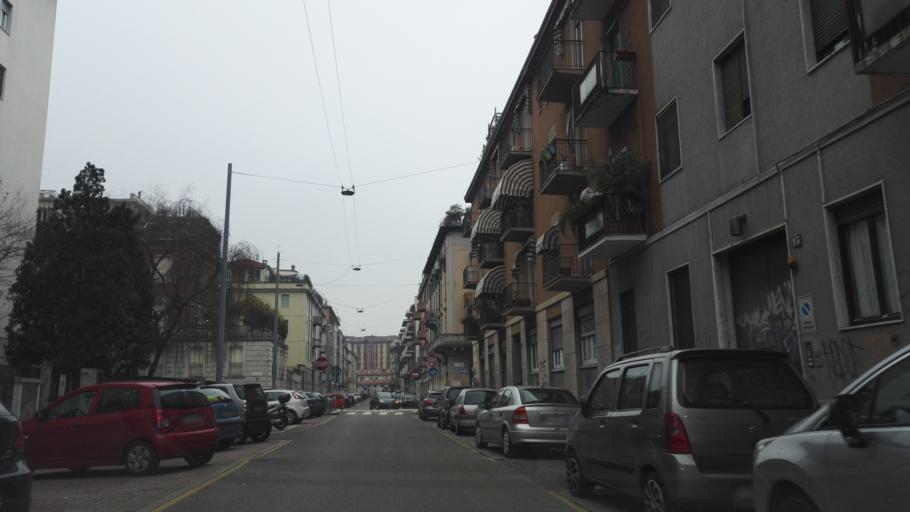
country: IT
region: Lombardy
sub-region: Citta metropolitana di Milano
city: Milano
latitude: 45.4453
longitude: 9.1815
